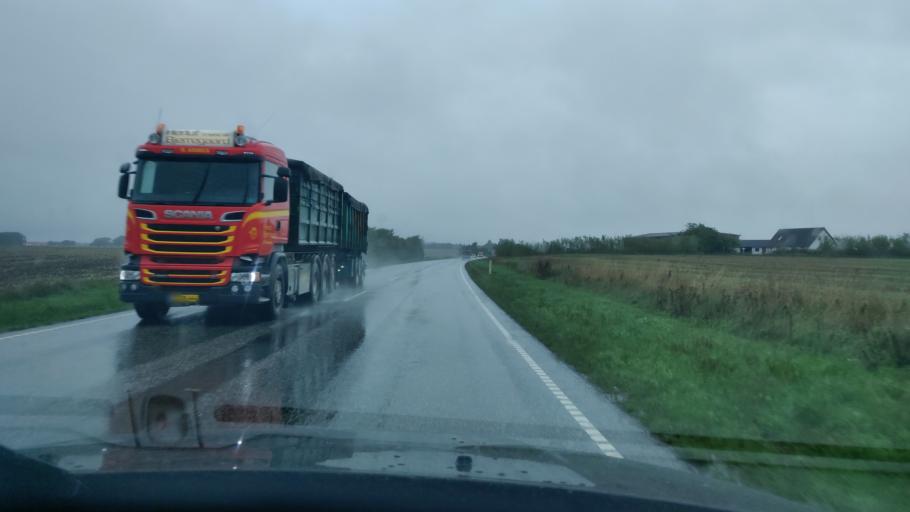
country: DK
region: North Denmark
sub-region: Thisted Kommune
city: Thisted
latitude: 56.9649
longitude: 8.6508
